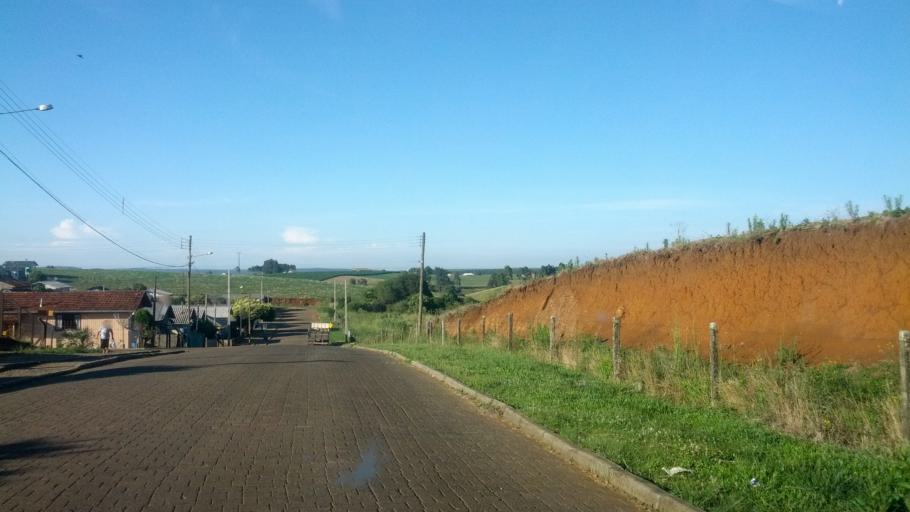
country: BR
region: Rio Grande do Sul
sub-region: Vacaria
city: Estrela
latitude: -27.9000
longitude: -50.7688
